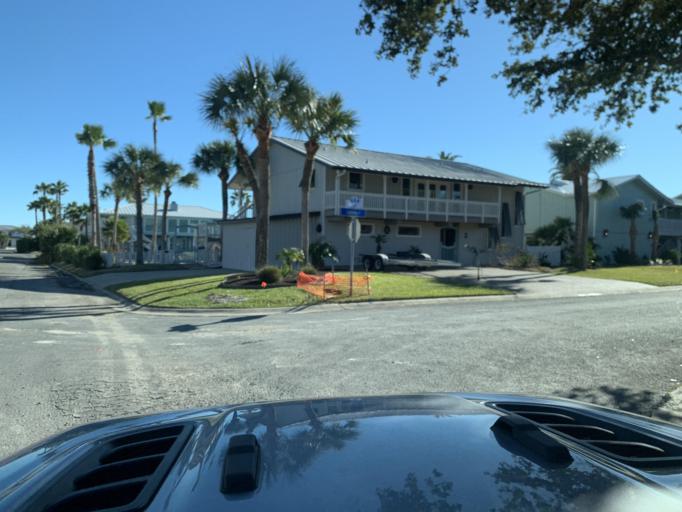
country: US
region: Texas
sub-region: Aransas County
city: Fulton
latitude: 28.0373
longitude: -97.0298
